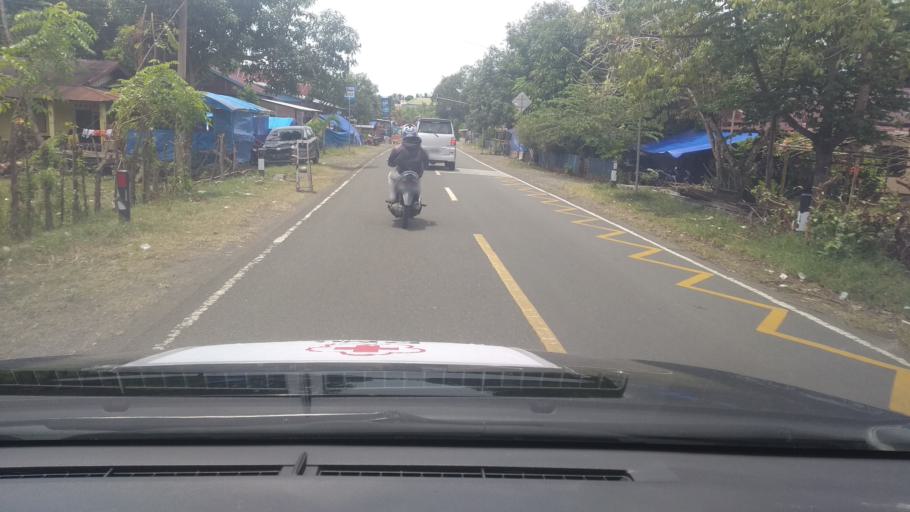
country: ID
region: Sulawesi Barat
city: Tapalang
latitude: -2.8464
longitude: 118.8589
